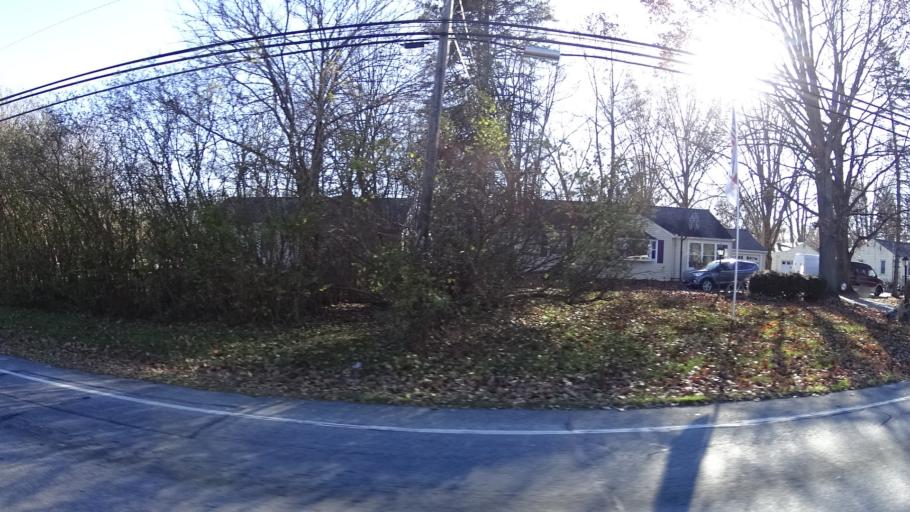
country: US
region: Ohio
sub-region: Lorain County
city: Elyria
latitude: 41.3366
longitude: -82.1247
